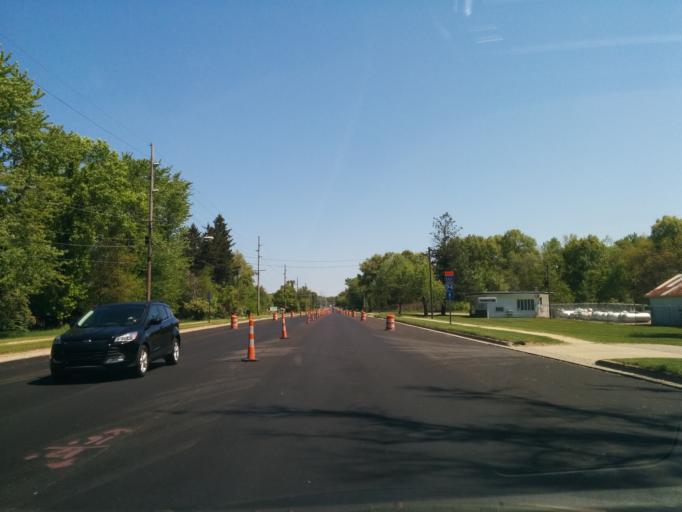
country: US
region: Michigan
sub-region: Berrien County
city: Bridgman
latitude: 41.9331
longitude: -86.5696
